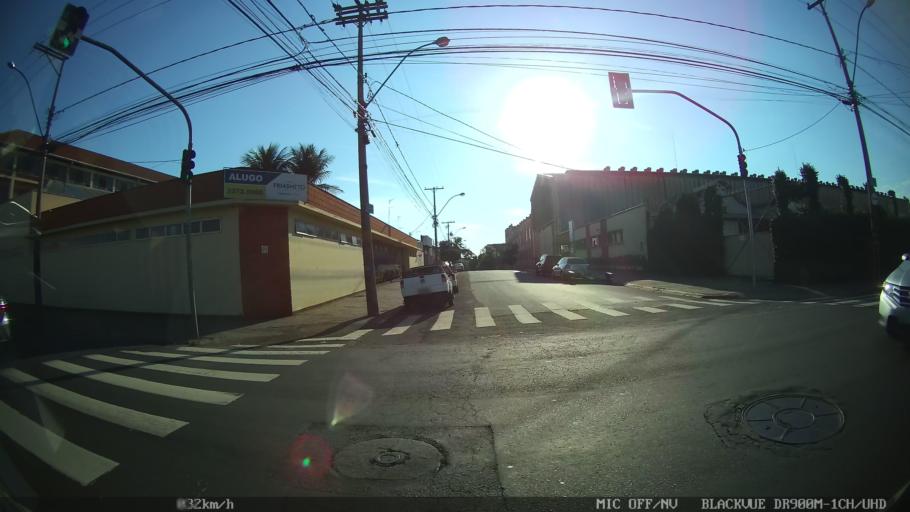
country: BR
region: Sao Paulo
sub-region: Piracicaba
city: Piracicaba
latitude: -22.7084
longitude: -47.6542
